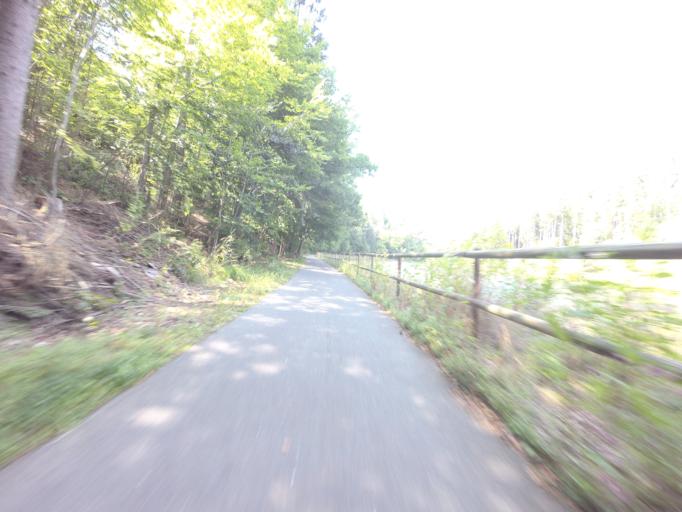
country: CZ
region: Jihocesky
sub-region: Okres Ceske Budejovice
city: Hluboka nad Vltavou
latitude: 49.0720
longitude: 14.4553
